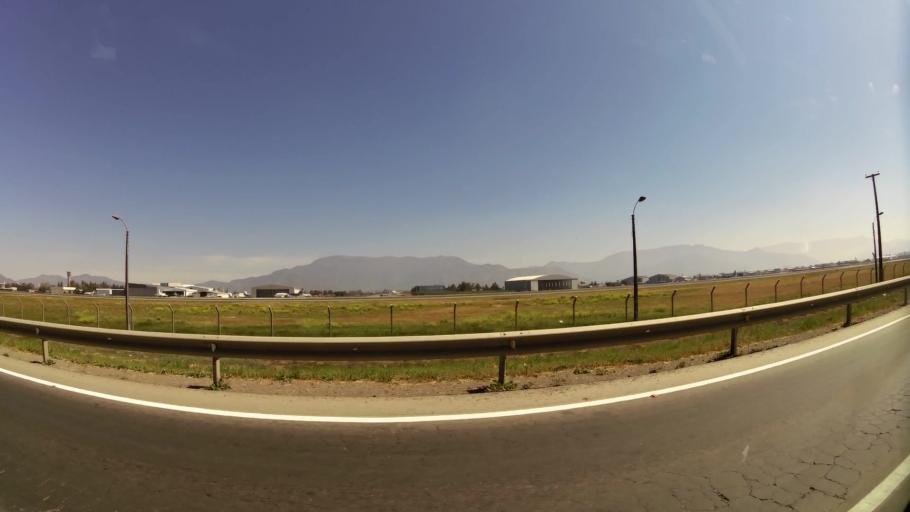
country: CL
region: Santiago Metropolitan
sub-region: Provincia de Santiago
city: Lo Prado
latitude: -33.3826
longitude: -70.7841
